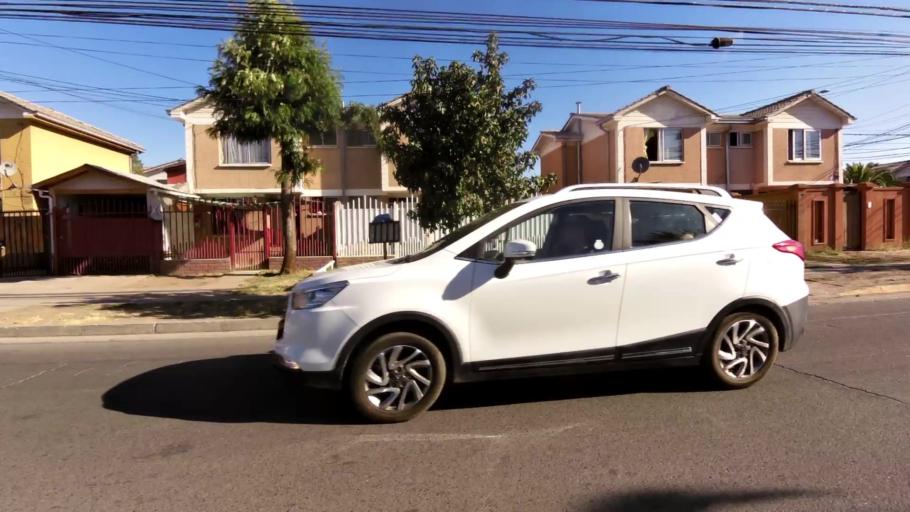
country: CL
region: O'Higgins
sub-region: Provincia de Cachapoal
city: Rancagua
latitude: -34.1775
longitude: -70.7576
